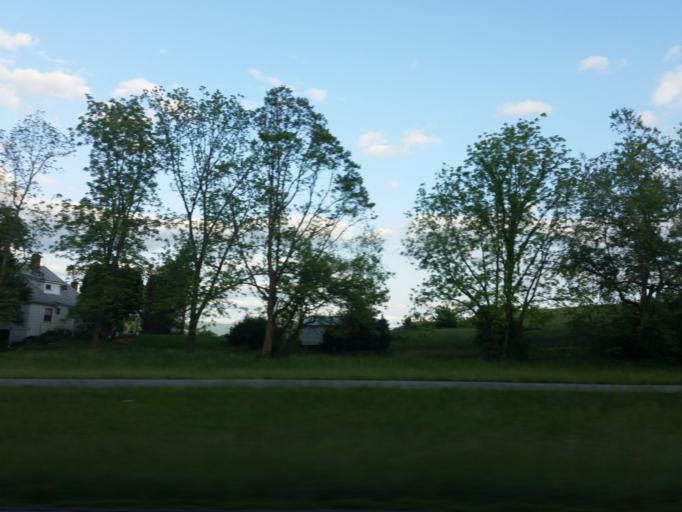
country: US
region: Virginia
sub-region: Washington County
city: Abingdon
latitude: 36.6586
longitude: -82.0679
